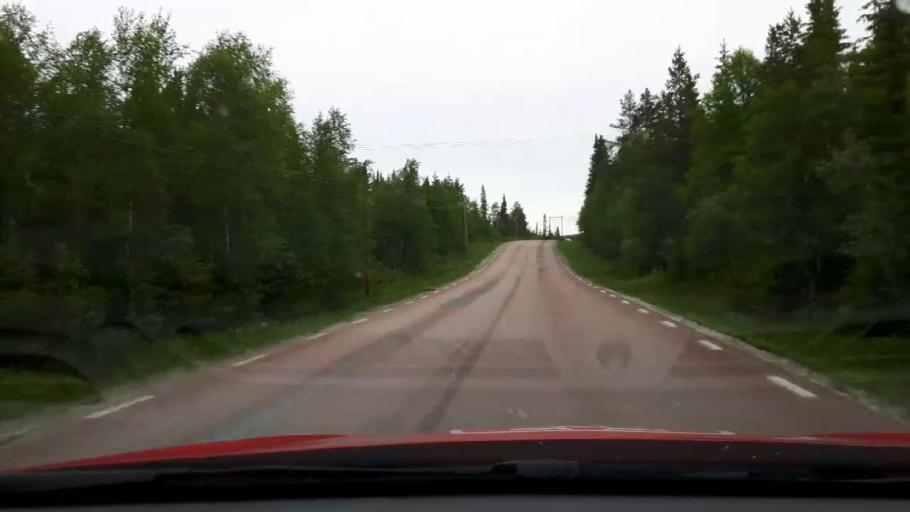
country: SE
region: Jaemtland
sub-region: Are Kommun
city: Are
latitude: 62.5607
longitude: 12.5665
